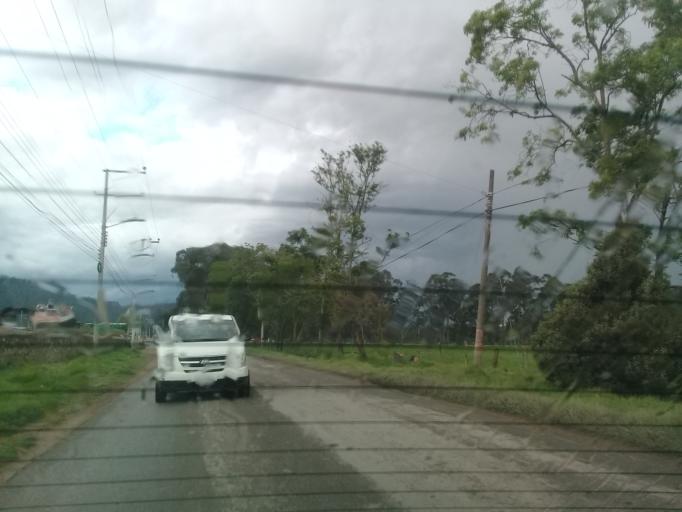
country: CO
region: Cundinamarca
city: Zipaquira
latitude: 5.0070
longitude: -73.9839
